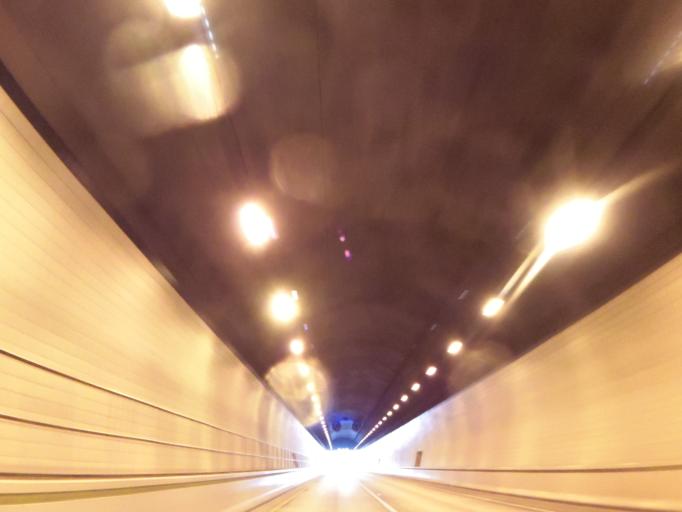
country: US
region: Tennessee
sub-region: Claiborne County
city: Harrogate
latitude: 36.6002
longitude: -83.6788
